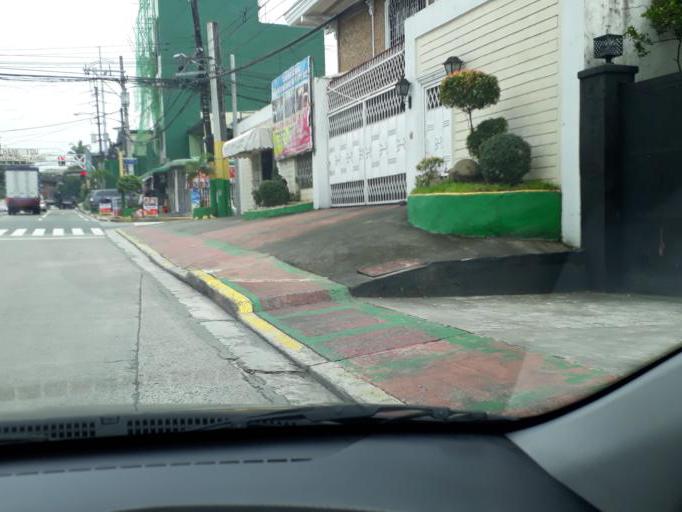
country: PH
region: Metro Manila
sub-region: Quezon City
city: Quezon City
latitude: 14.6310
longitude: 121.0502
